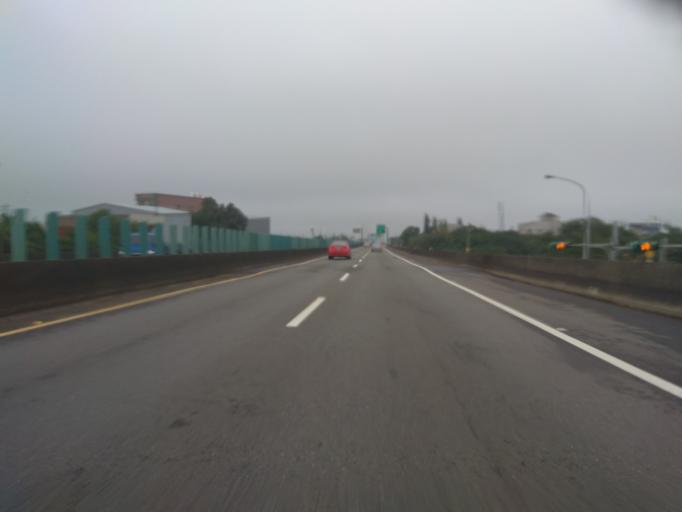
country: TW
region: Taiwan
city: Taoyuan City
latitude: 24.9853
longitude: 121.1272
